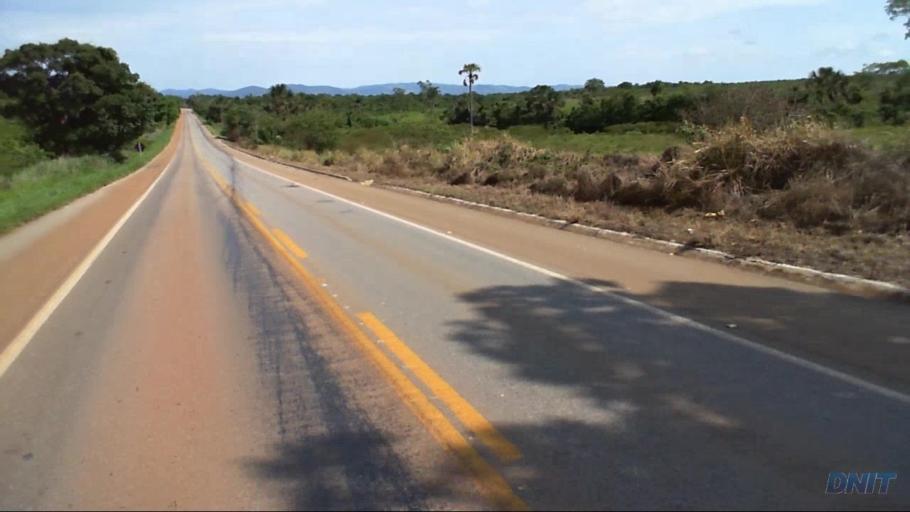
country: BR
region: Goias
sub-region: Barro Alto
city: Barro Alto
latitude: -15.0974
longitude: -48.8528
